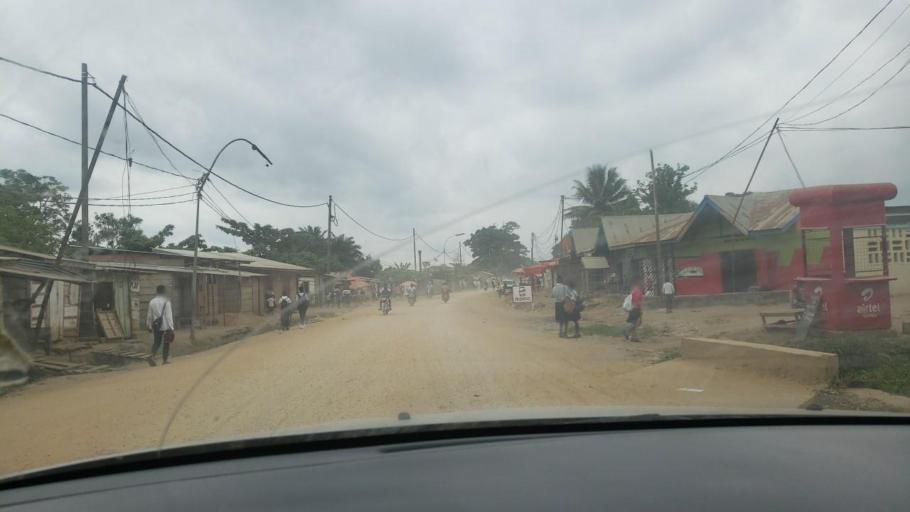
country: CD
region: Eastern Province
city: Kisangani
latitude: 0.5096
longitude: 25.2129
